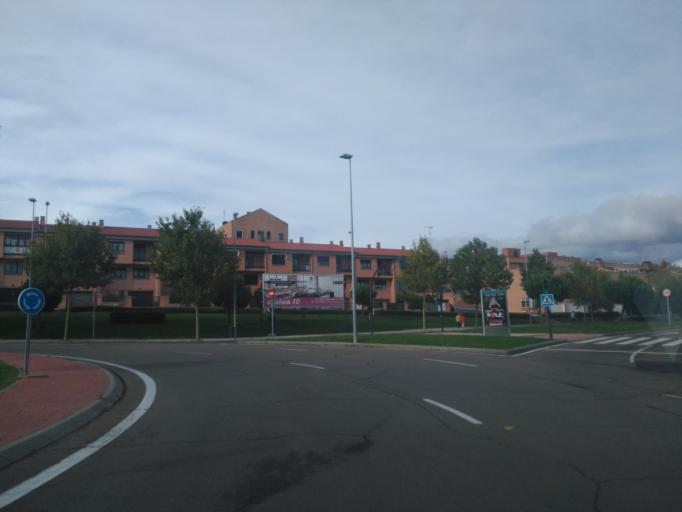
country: ES
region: Castille and Leon
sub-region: Provincia de Salamanca
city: Salamanca
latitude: 40.9644
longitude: -5.6462
